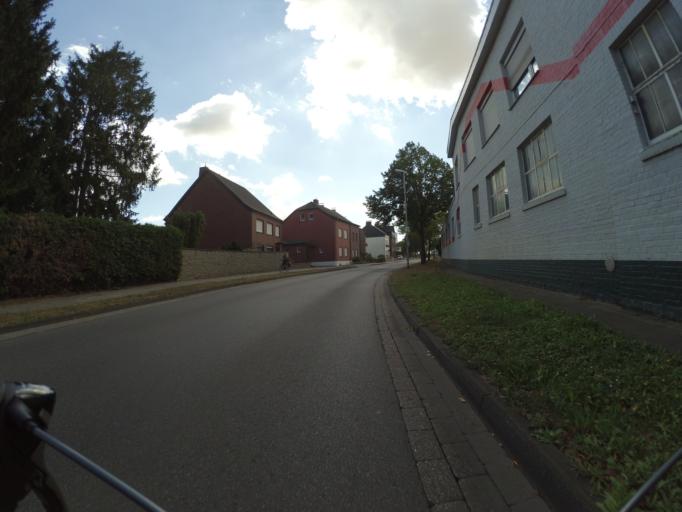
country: DE
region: North Rhine-Westphalia
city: Julich
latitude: 50.8959
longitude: 6.3587
